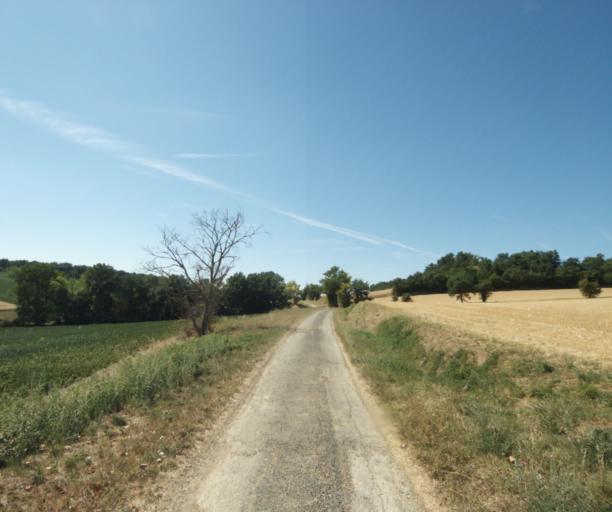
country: FR
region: Midi-Pyrenees
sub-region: Departement de la Haute-Garonne
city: Saint-Felix-Lauragais
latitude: 43.4985
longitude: 1.9333
